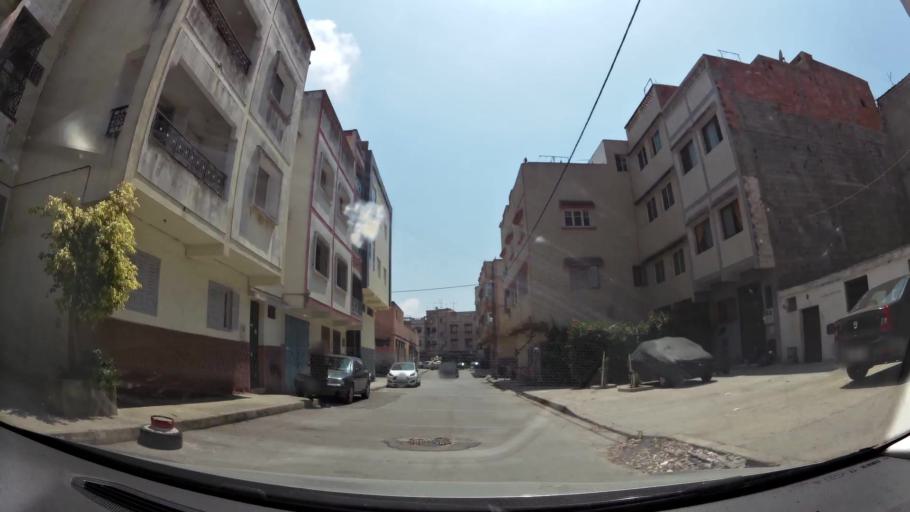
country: MA
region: Rabat-Sale-Zemmour-Zaer
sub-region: Skhirate-Temara
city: Temara
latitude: 33.9723
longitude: -6.8907
